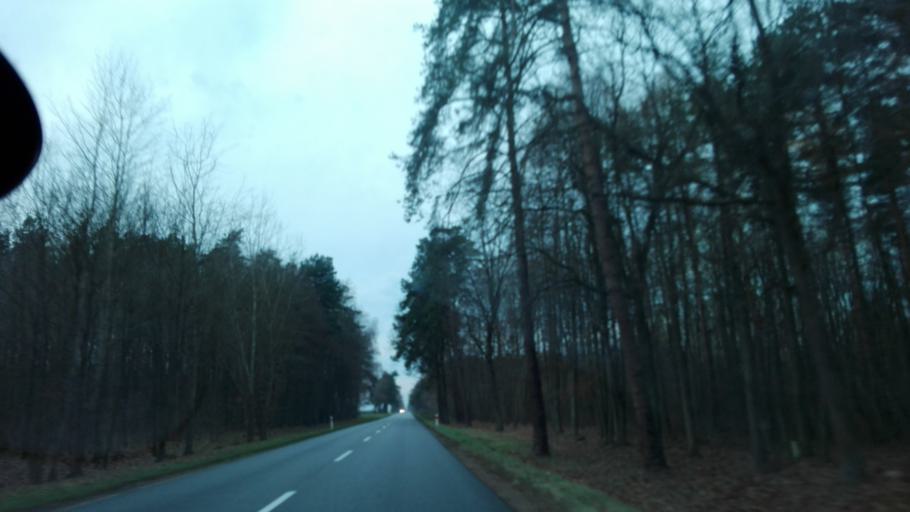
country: PL
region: Lublin Voivodeship
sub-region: Powiat radzynski
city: Wohyn
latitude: 51.7782
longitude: 22.8347
